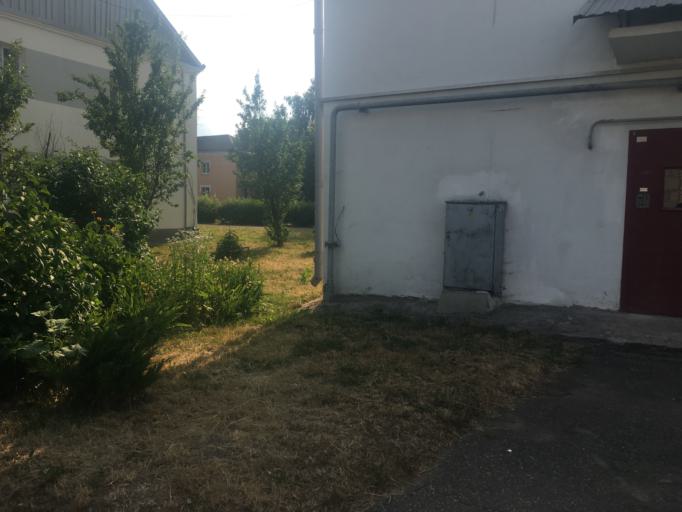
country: BY
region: Grodnenskaya
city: Hrodna
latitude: 53.6657
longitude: 23.8016
